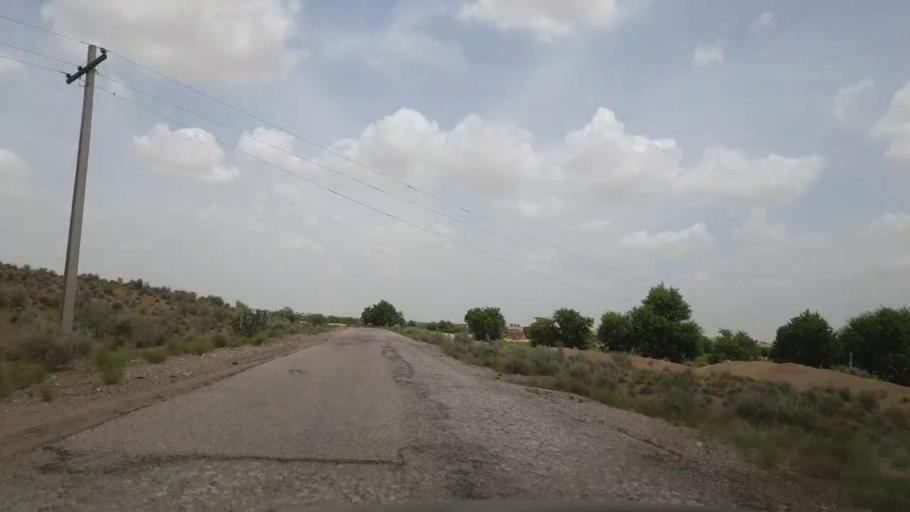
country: PK
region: Sindh
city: Kot Diji
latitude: 27.2007
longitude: 69.1262
